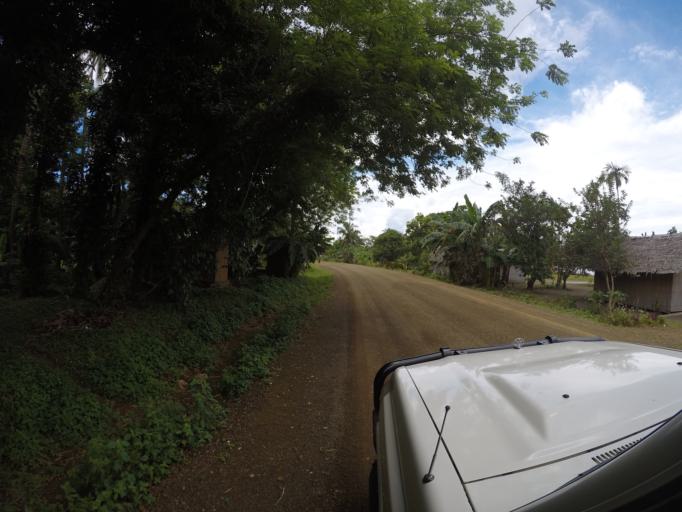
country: PG
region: Milne Bay
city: Alotau
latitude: -10.3387
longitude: 150.6456
